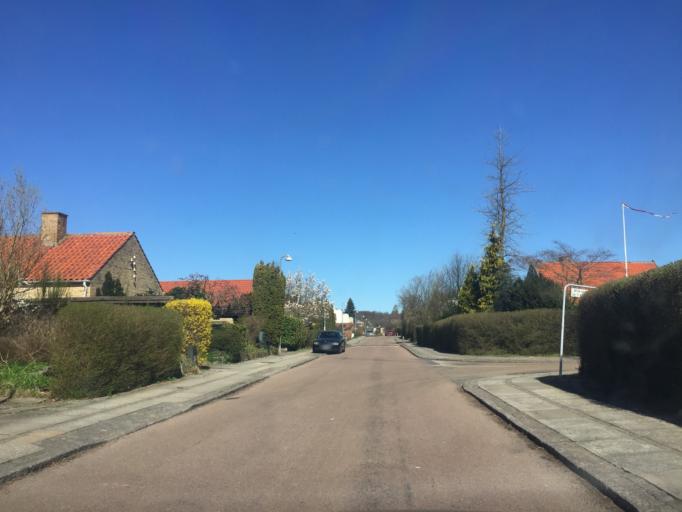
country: DK
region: Capital Region
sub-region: Rudersdal Kommune
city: Holte
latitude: 55.7922
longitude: 12.4810
